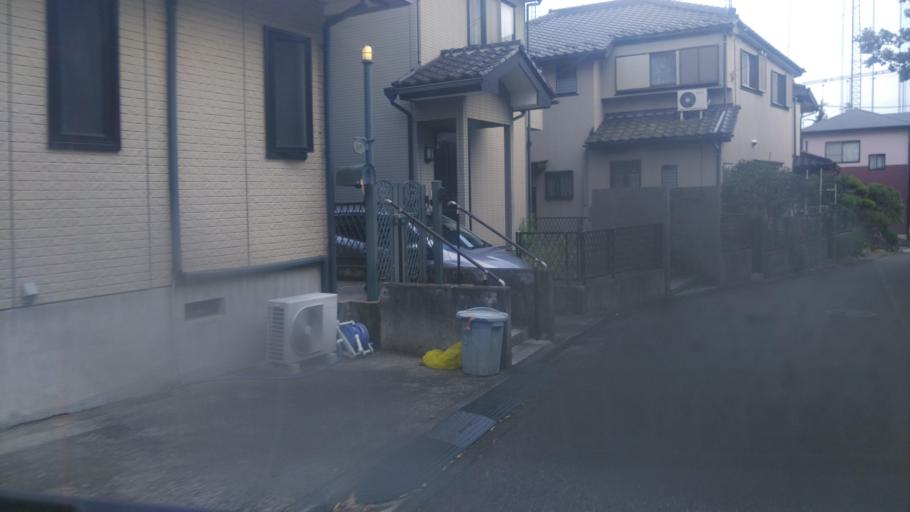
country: JP
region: Kanagawa
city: Fujisawa
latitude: 35.3945
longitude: 139.4369
